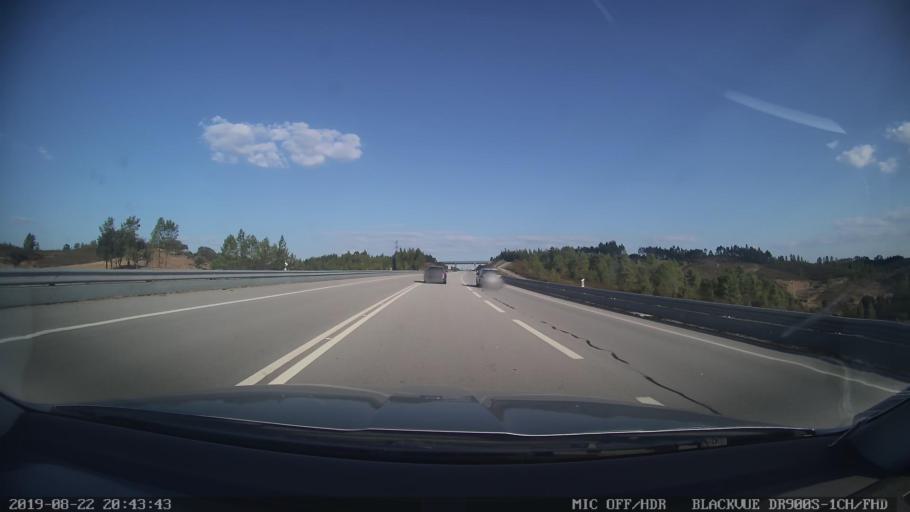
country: PT
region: Castelo Branco
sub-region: Proenca-A-Nova
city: Proenca-a-Nova
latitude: 39.7005
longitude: -7.8372
